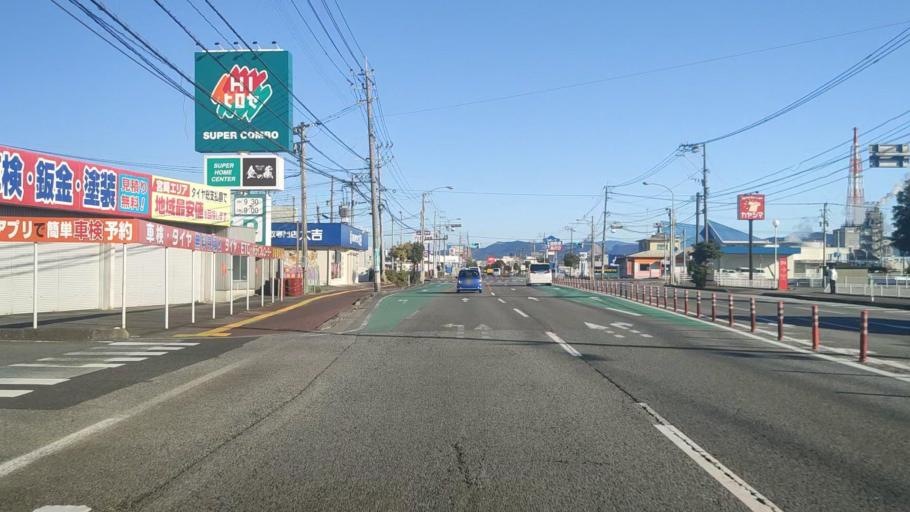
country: JP
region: Miyazaki
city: Nobeoka
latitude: 32.5617
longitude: 131.6811
